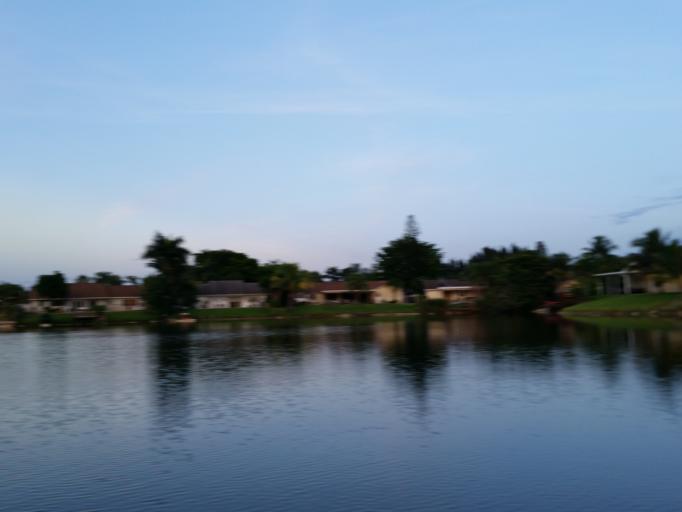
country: US
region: Florida
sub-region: Broward County
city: Cooper City
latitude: 26.0581
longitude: -80.2623
